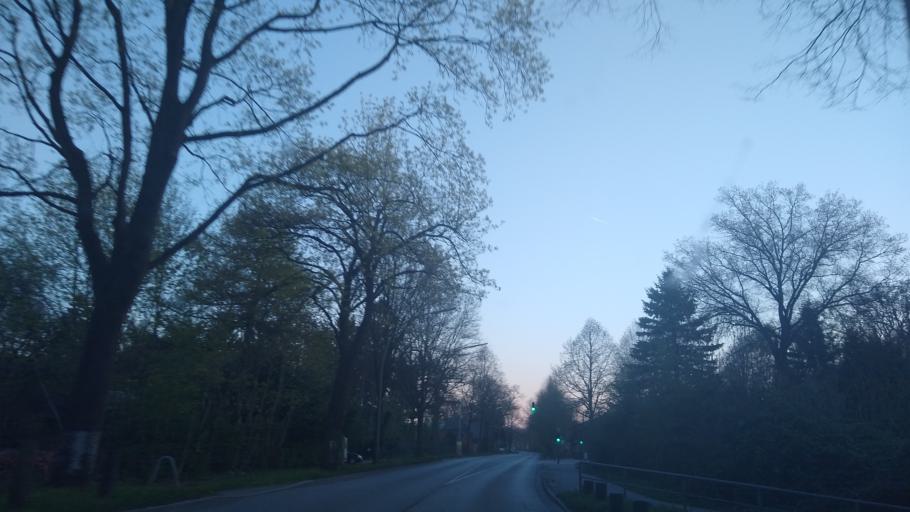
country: DE
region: Schleswig-Holstein
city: Bonningstedt
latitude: 53.6494
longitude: 9.9071
